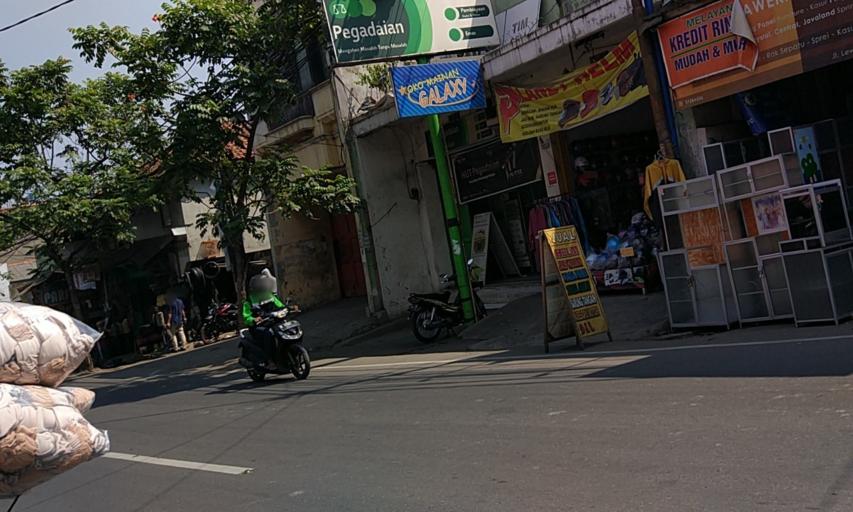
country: ID
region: West Java
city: Cimahi
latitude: -6.8977
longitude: 107.5571
